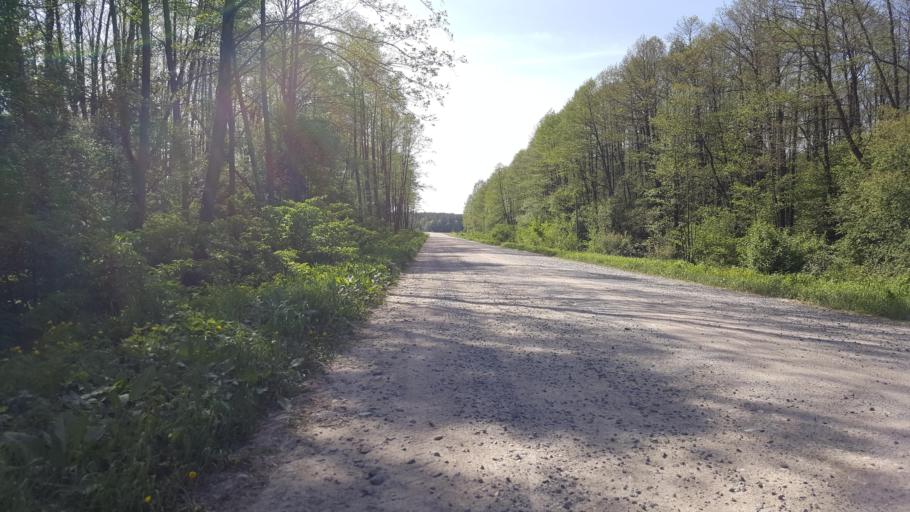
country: BY
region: Brest
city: Zhabinka
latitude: 52.3144
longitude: 24.0283
